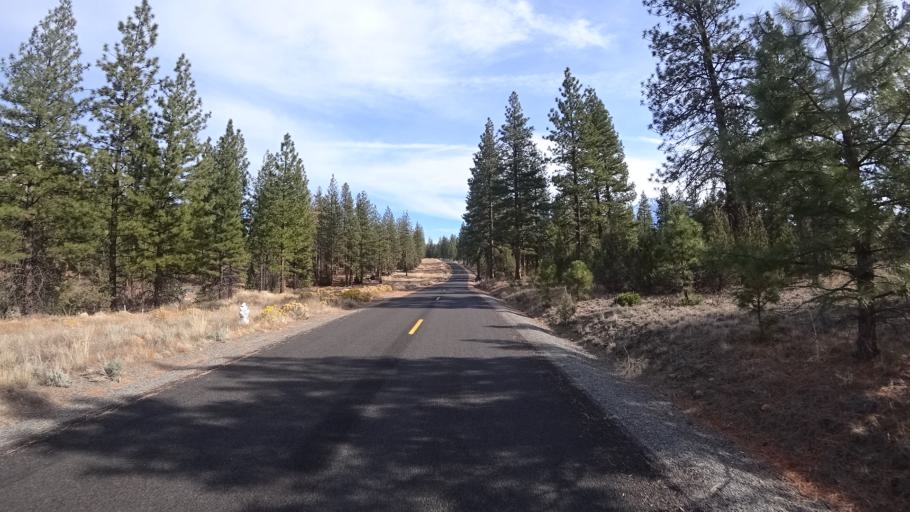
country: US
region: California
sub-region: Siskiyou County
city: Weed
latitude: 41.4980
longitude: -122.3869
